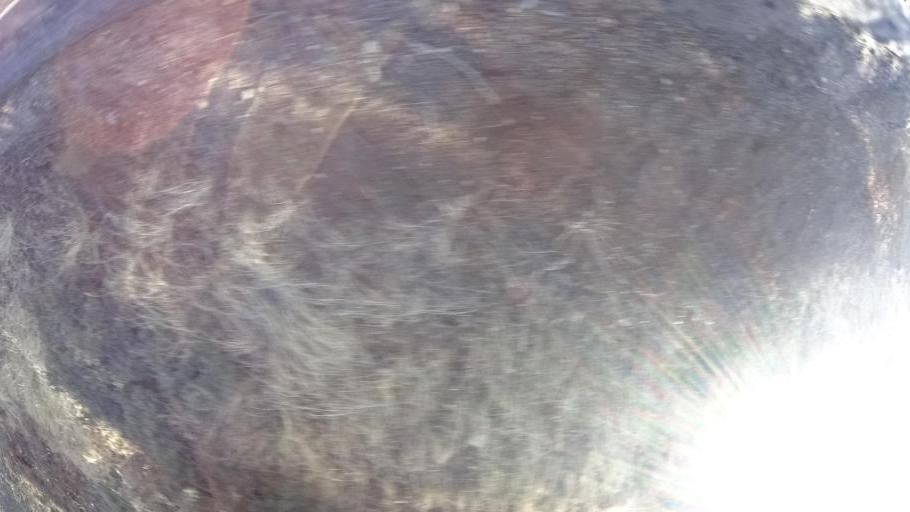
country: US
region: California
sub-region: Kern County
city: Pine Mountain Club
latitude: 34.8786
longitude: -119.3426
